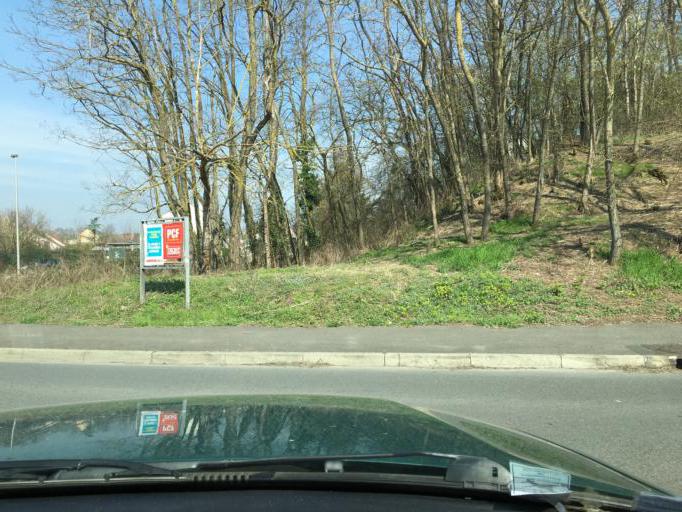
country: FR
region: Centre
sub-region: Departement du Loiret
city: Fleury-les-Aubrais
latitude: 47.9462
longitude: 1.9030
